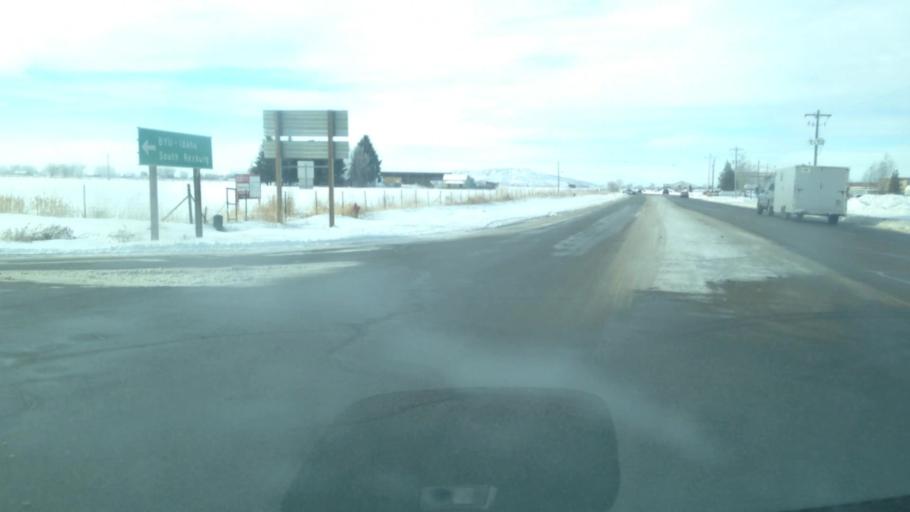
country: US
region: Idaho
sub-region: Madison County
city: Rexburg
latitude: 43.8046
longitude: -111.8142
